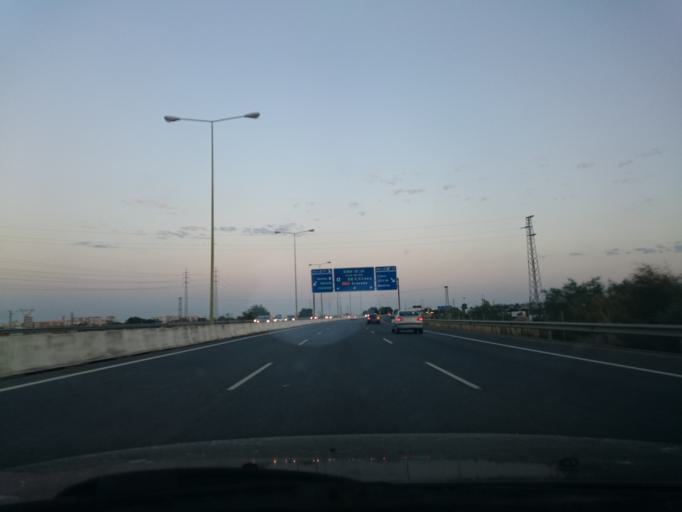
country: ES
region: Andalusia
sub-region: Provincia de Sevilla
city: Camas
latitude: 37.3981
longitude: -6.0262
